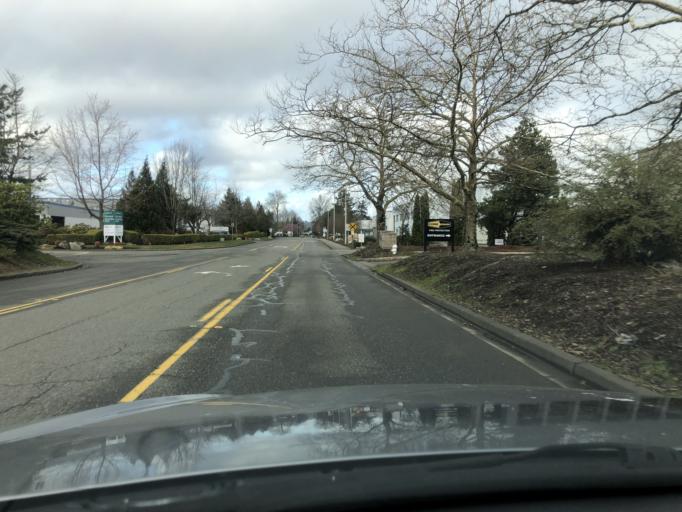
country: US
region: Washington
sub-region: King County
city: Tukwila
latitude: 47.4340
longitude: -122.2439
